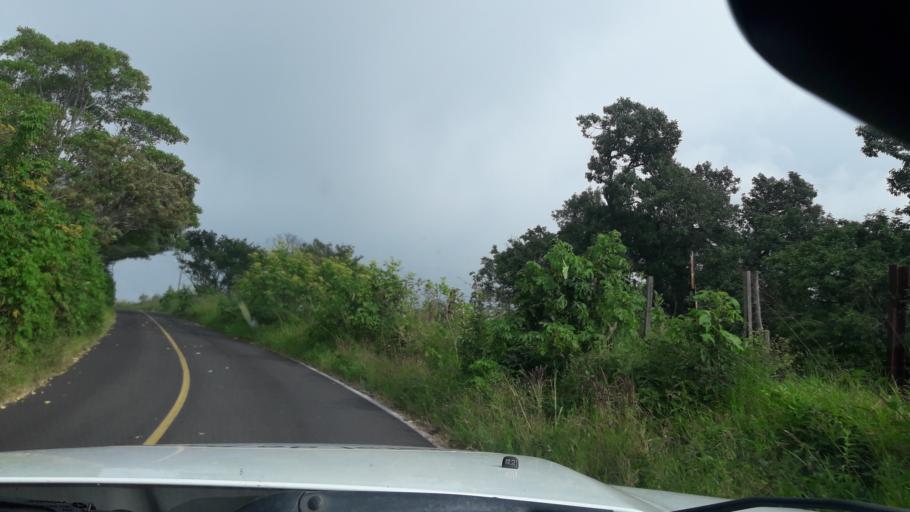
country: MX
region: Colima
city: Queseria
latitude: 19.4087
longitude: -103.6325
